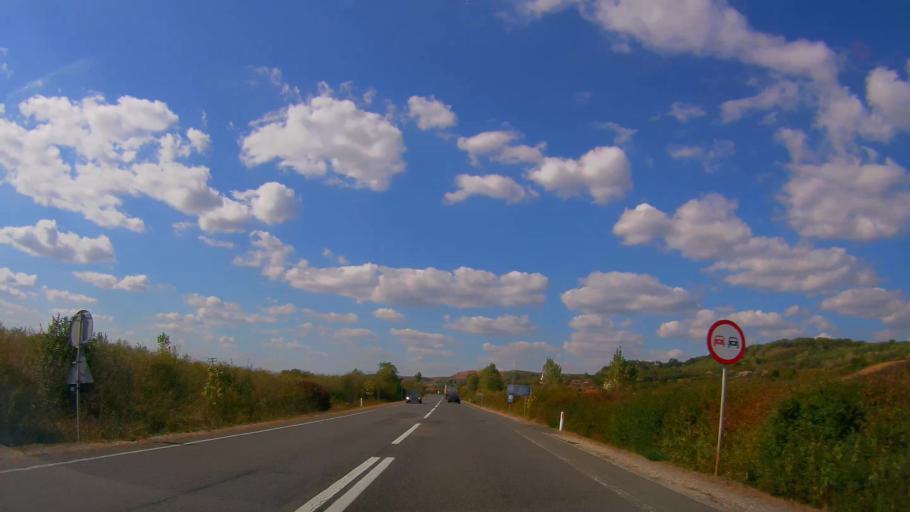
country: RO
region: Salaj
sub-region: Comuna Bocsa
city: Bocsa
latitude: 47.3139
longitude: 22.9123
